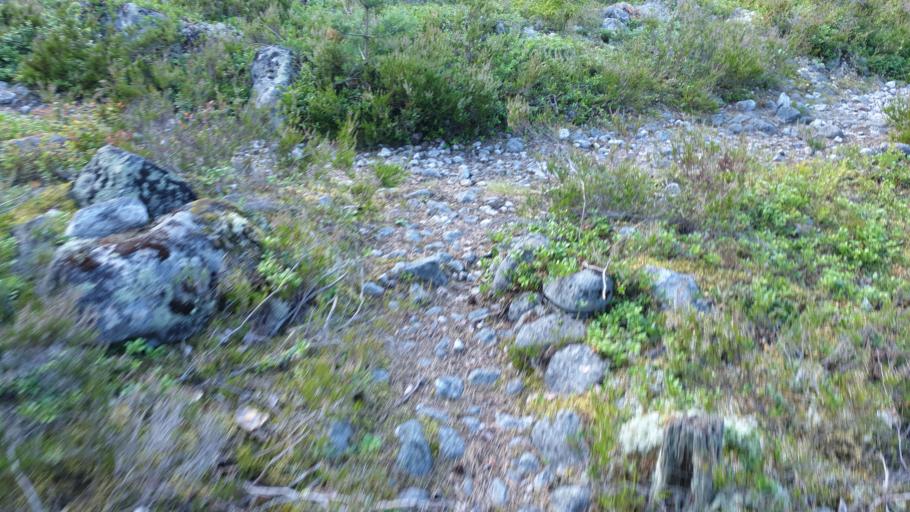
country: SE
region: Gaevleborg
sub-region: Soderhamns Kommun
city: Marielund
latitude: 61.4238
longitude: 17.1535
